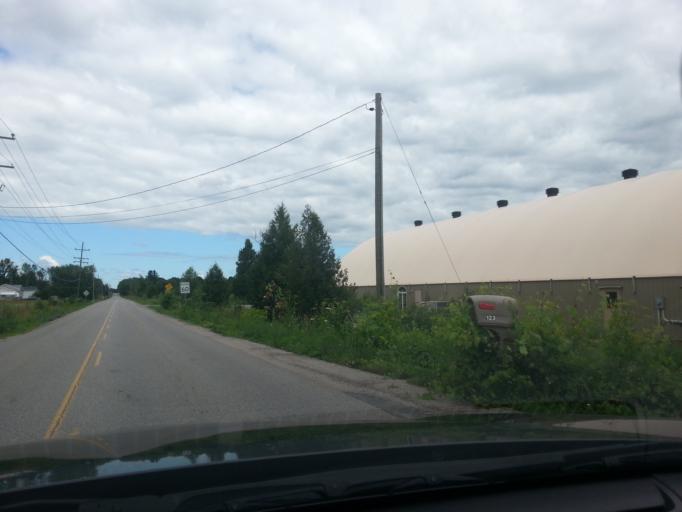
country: CA
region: Ontario
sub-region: Lanark County
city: Smiths Falls
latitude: 44.8760
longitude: -76.0418
